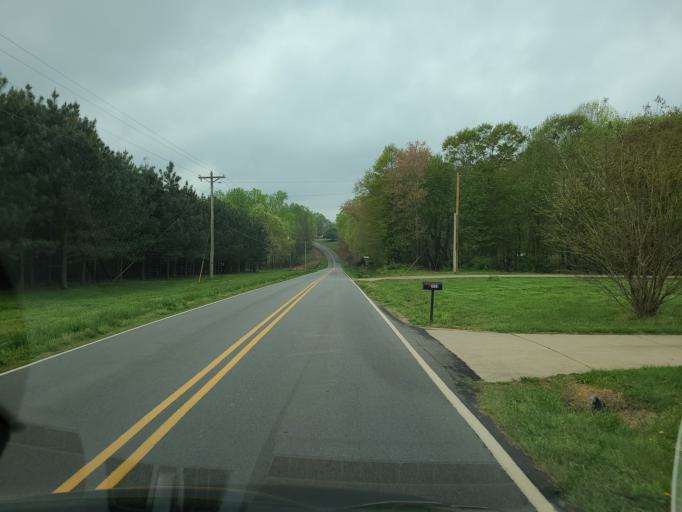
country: US
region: North Carolina
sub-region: Gaston County
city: Cherryville
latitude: 35.4512
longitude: -81.3577
